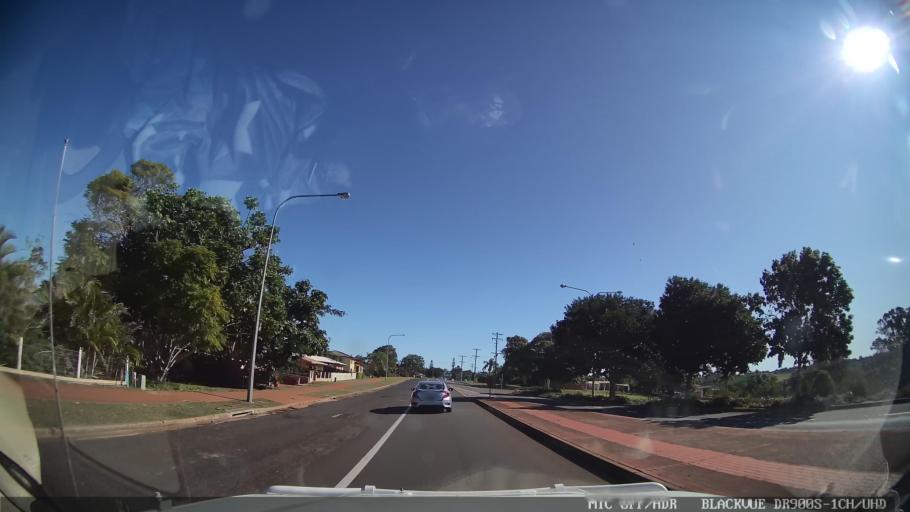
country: AU
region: Queensland
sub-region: Bundaberg
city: Childers
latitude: -25.2330
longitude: 152.2702
